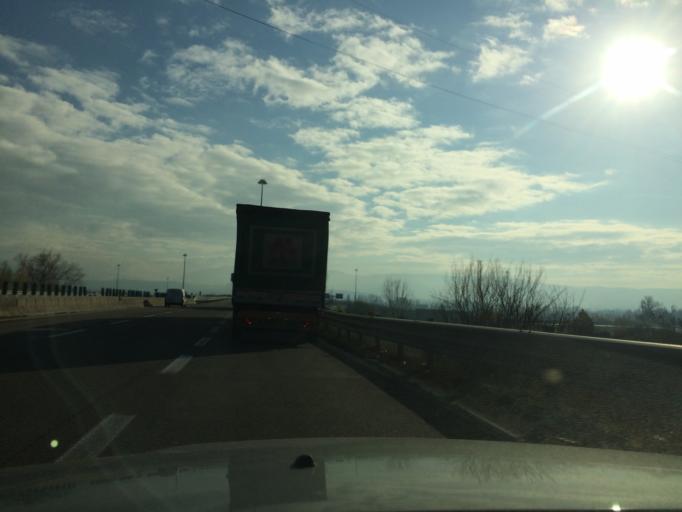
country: IT
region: Umbria
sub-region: Provincia di Terni
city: San Gemini
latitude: 42.5729
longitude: 12.5749
